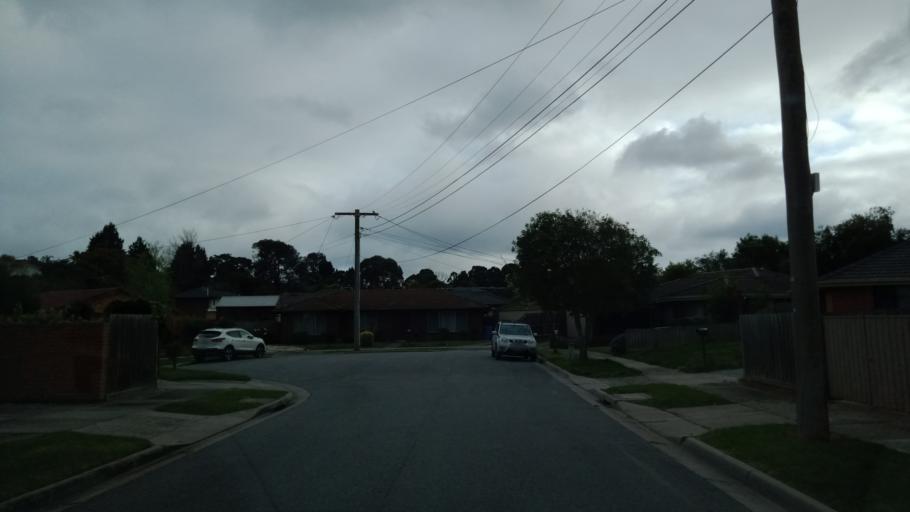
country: AU
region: Victoria
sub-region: Casey
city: Eumemmerring
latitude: -37.9913
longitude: 145.2500
